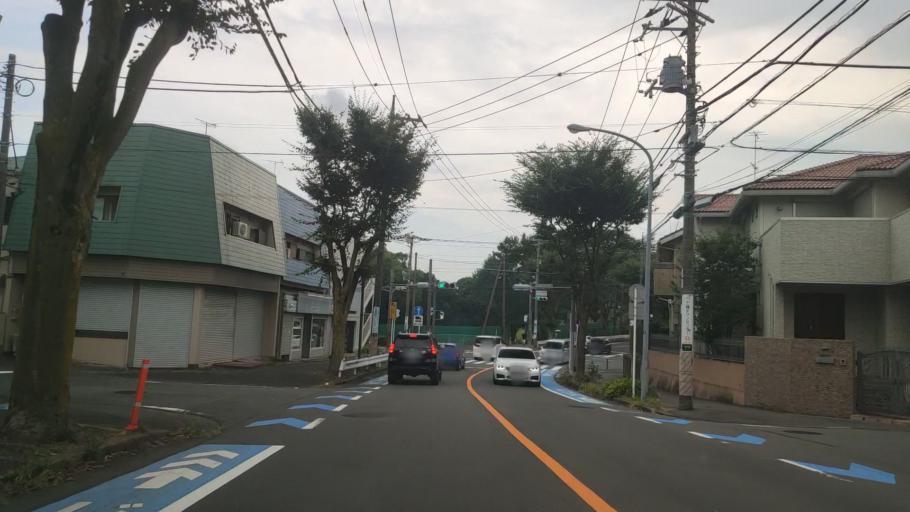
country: JP
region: Tokyo
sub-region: Machida-shi
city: Machida
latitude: 35.5122
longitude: 139.4564
